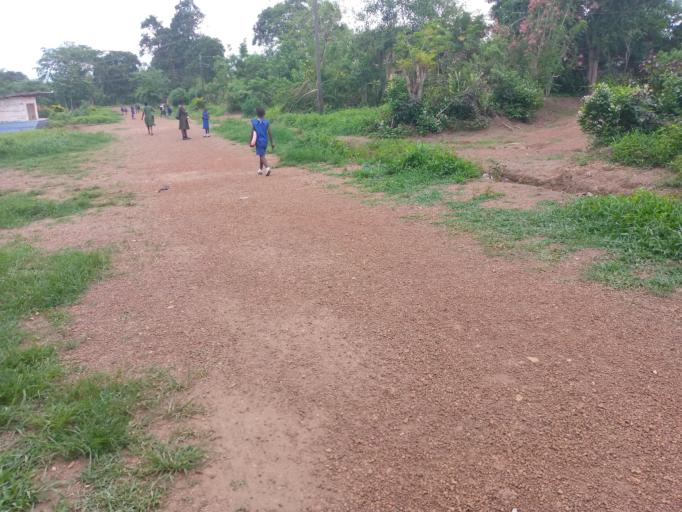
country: SL
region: Southern Province
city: Largo
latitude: 8.1122
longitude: -12.0694
